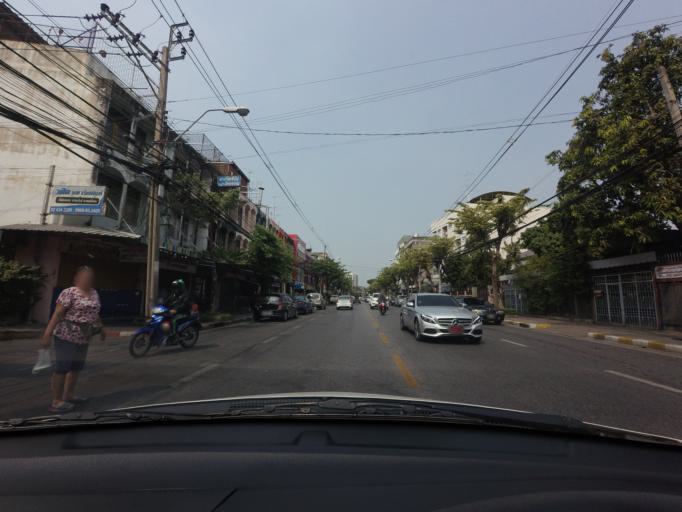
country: TH
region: Bangkok
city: Bangkok Noi
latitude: 13.7671
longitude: 100.4712
